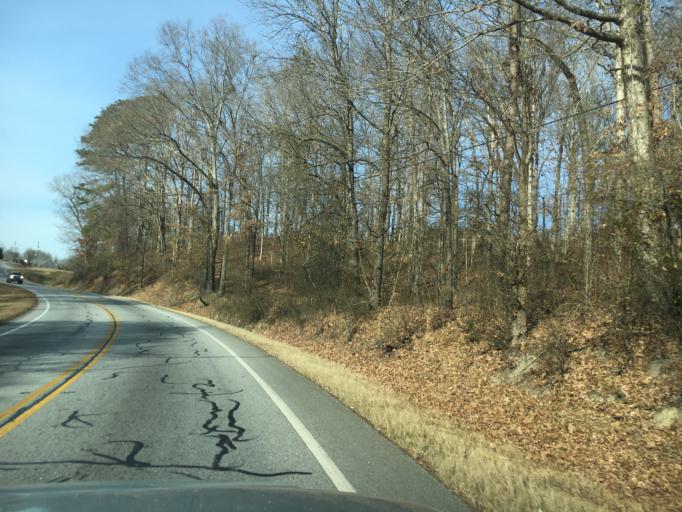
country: US
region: Georgia
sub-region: Jackson County
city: Hoschton
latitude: 34.0640
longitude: -83.7198
